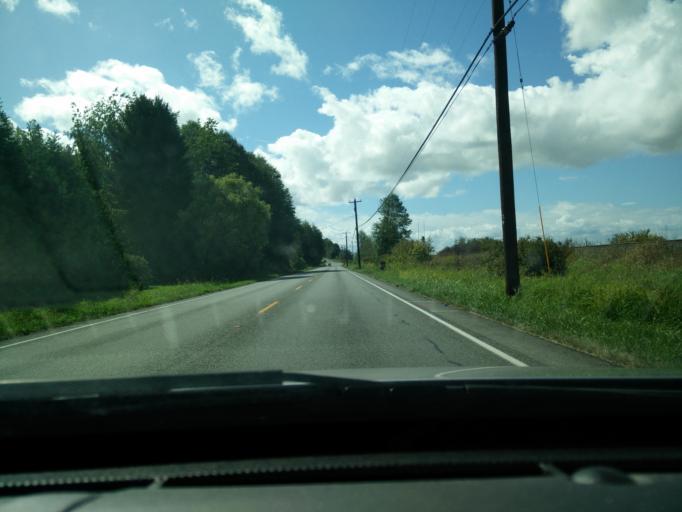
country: US
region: Washington
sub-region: Snohomish County
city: Stanwood
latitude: 48.2794
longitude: -122.3613
